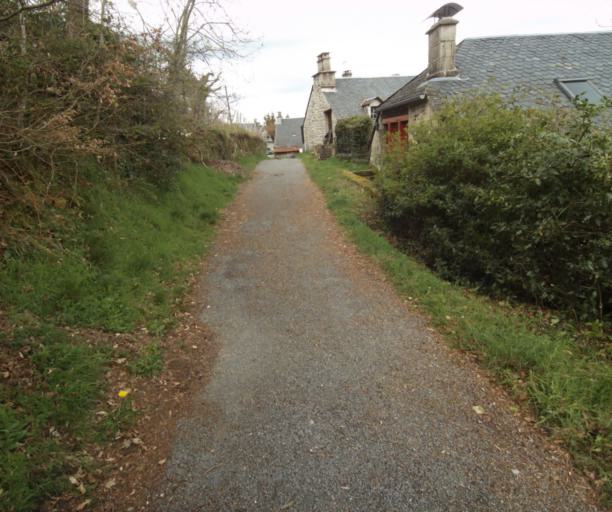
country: FR
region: Limousin
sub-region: Departement de la Correze
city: Argentat
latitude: 45.1910
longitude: 1.9592
